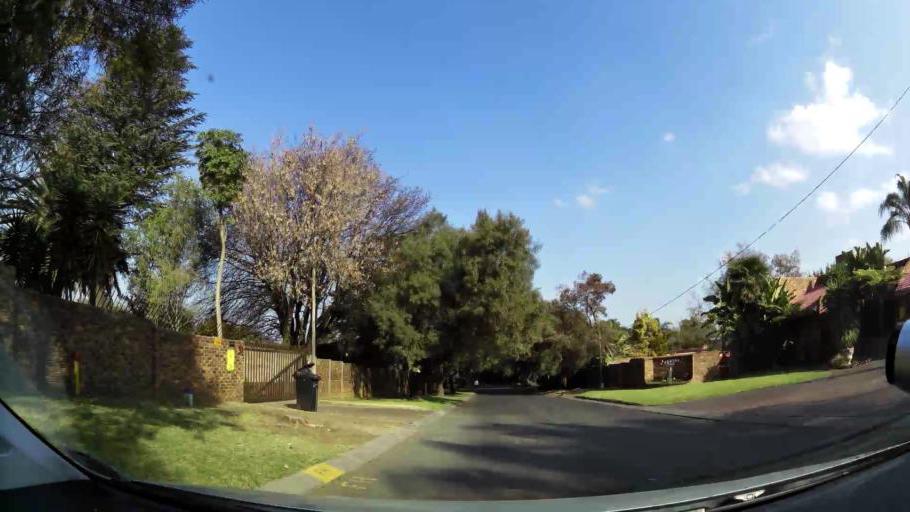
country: ZA
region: Gauteng
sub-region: City of Johannesburg Metropolitan Municipality
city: Modderfontein
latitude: -26.0812
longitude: 28.2023
